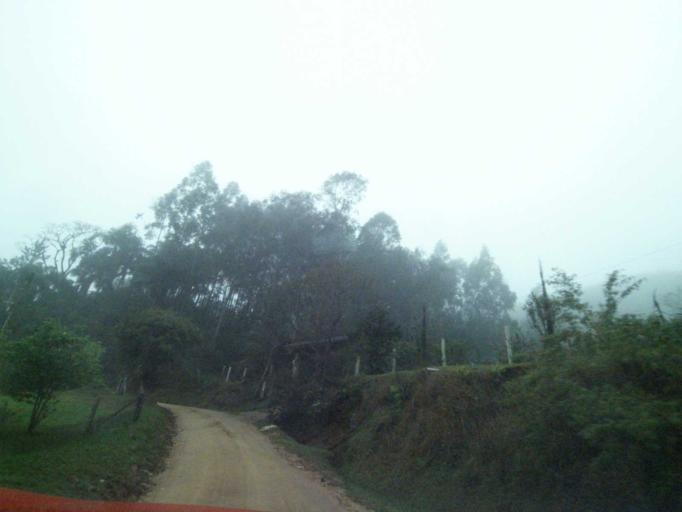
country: BR
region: Santa Catarina
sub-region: Anitapolis
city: Anitapolis
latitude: -27.9140
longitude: -49.1050
